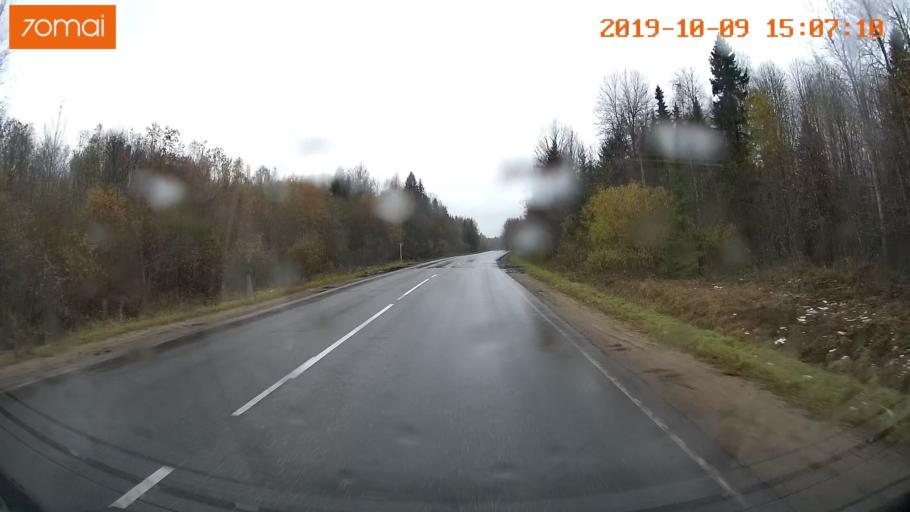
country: RU
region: Kostroma
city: Susanino
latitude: 58.2226
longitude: 41.6528
